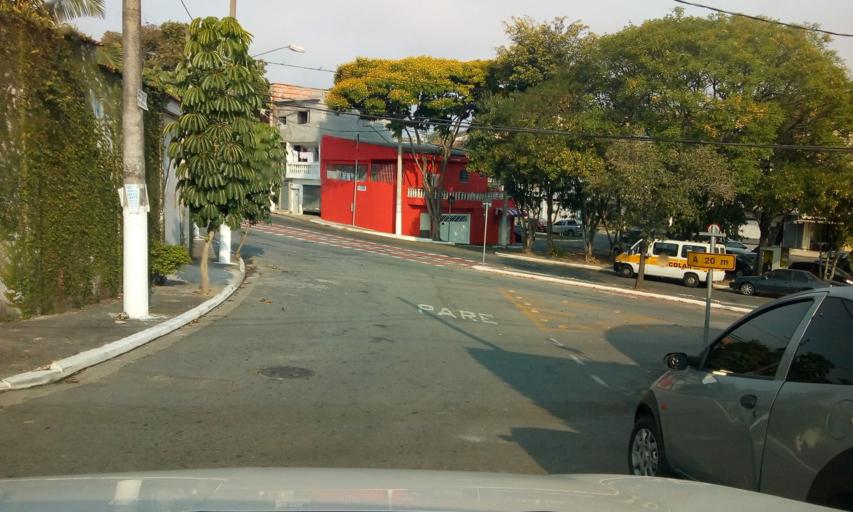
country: BR
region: Sao Paulo
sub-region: Diadema
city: Diadema
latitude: -23.7174
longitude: -46.6945
